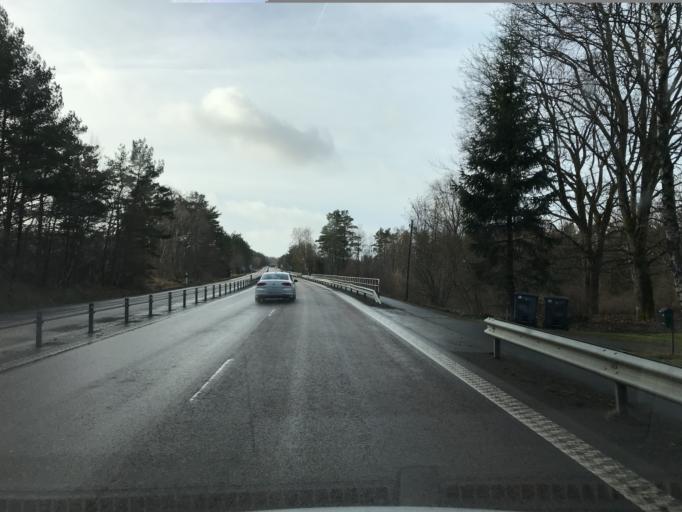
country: SE
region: Skane
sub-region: Perstorps Kommun
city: Perstorp
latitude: 56.1509
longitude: 13.5408
